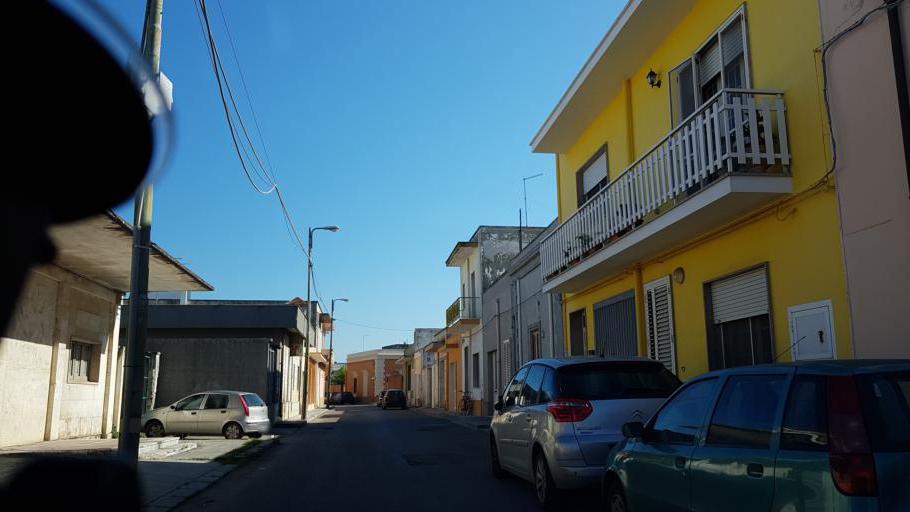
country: IT
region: Apulia
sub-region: Provincia di Brindisi
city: Torchiarolo
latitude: 40.4847
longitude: 18.0551
